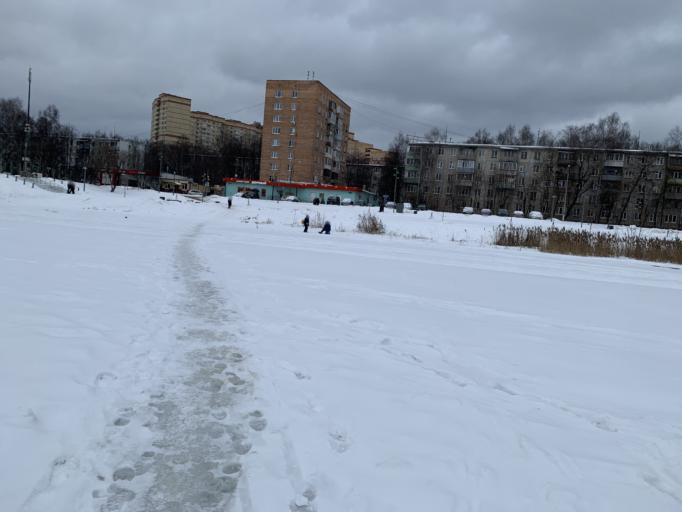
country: RU
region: Moskovskaya
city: Pushkino
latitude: 56.0061
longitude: 37.8643
